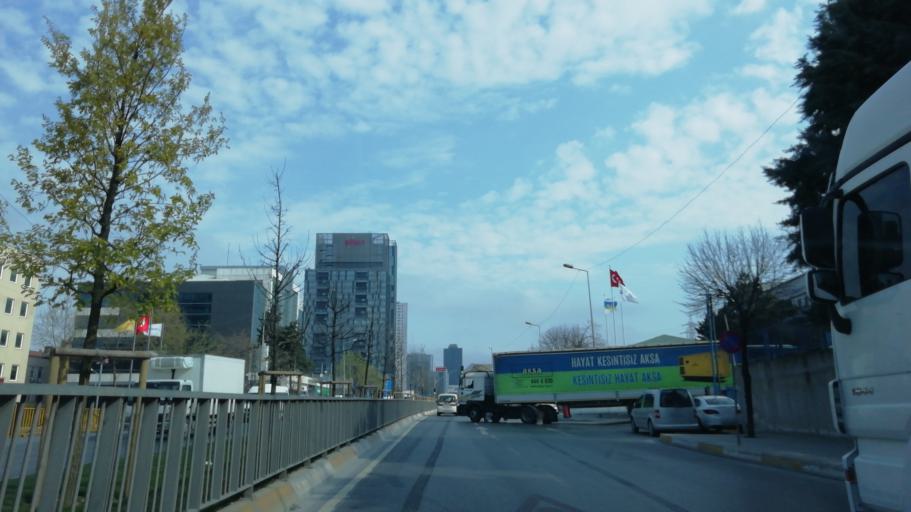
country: TR
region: Istanbul
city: Mahmutbey
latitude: 41.0485
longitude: 28.8123
